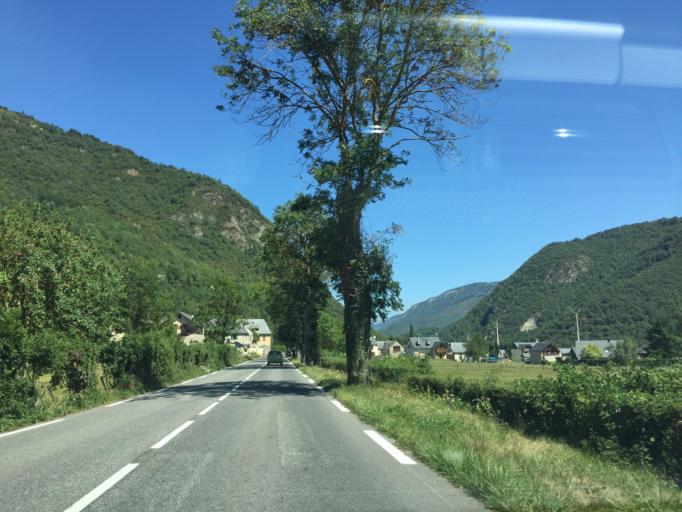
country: FR
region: Midi-Pyrenees
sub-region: Departement des Hautes-Pyrenees
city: Saint-Lary-Soulan
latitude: 42.8698
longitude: 0.3405
